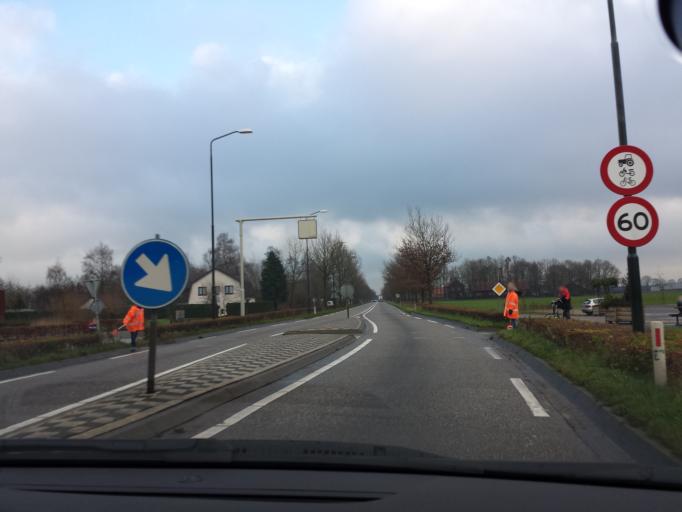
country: NL
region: North Brabant
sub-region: Gemeente Sint Anthonis
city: Sint Anthonis
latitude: 51.5473
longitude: 5.8132
